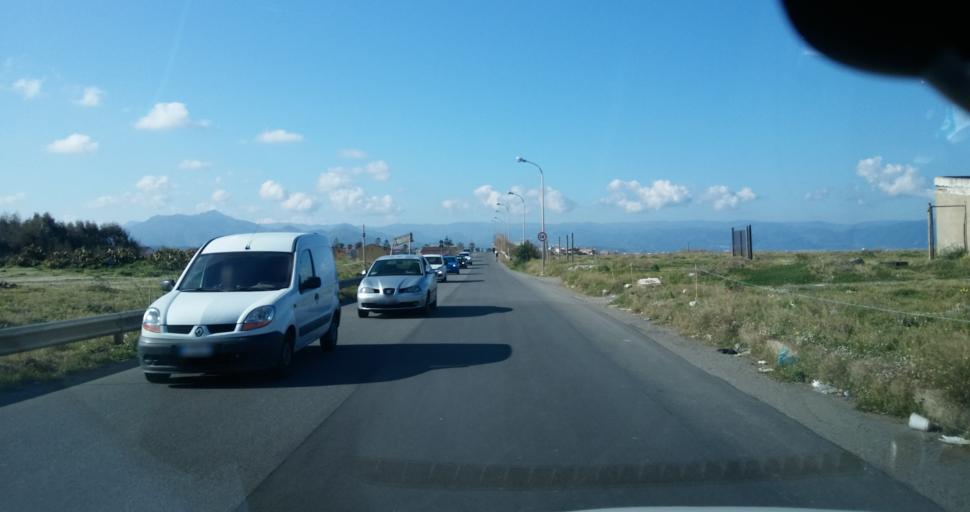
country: IT
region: Sicily
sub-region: Messina
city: Barcellona Pozzo di Gotto
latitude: 38.1846
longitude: 15.2122
